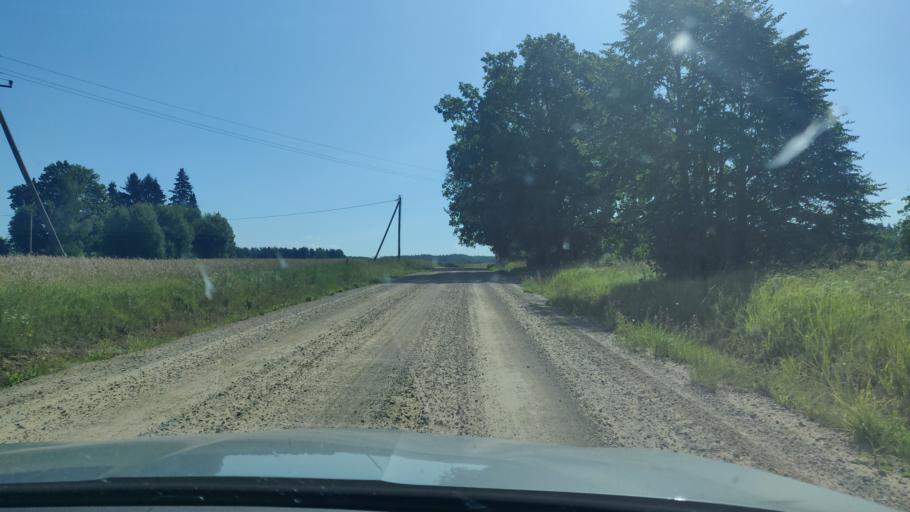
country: EE
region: Tartu
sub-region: Elva linn
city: Elva
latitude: 58.1357
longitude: 26.3955
